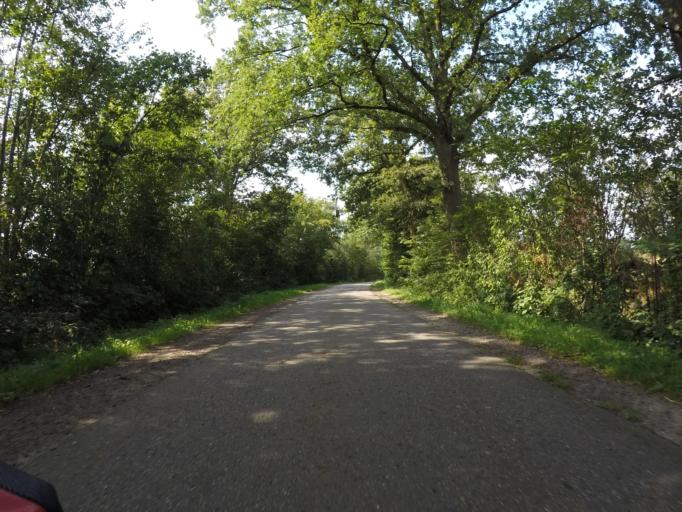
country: DE
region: Schleswig-Holstein
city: Kisdorf
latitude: 53.7769
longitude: 10.0356
